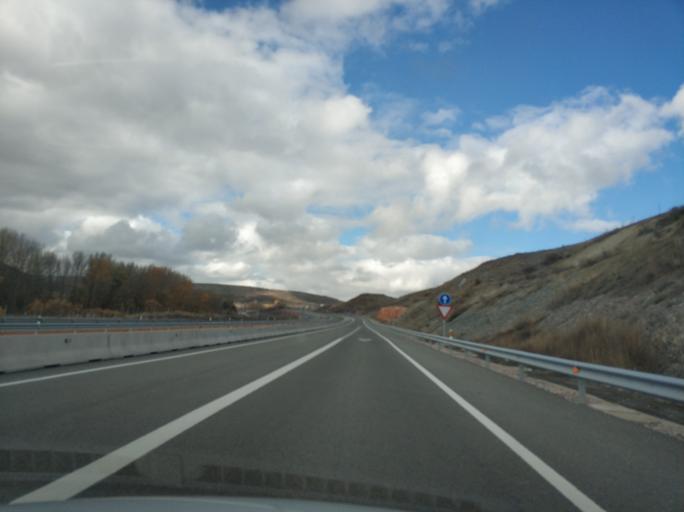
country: ES
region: Castille and Leon
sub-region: Provincia de Soria
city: Medinaceli
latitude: 41.1733
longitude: -2.4212
